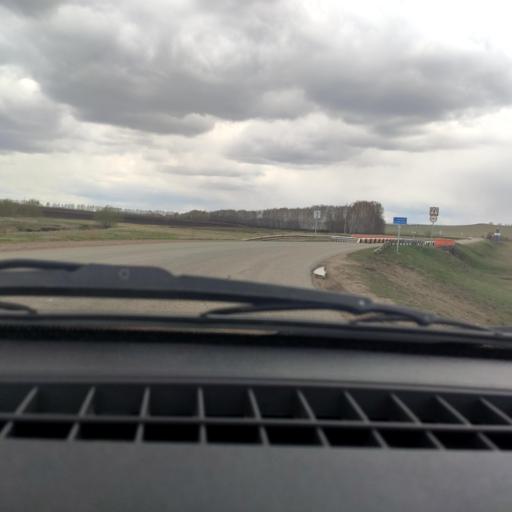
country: RU
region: Bashkortostan
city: Chekmagush
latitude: 55.1162
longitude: 54.7525
